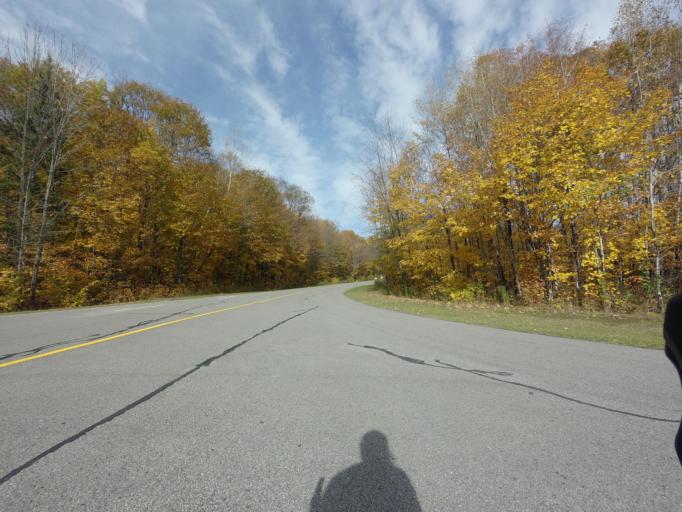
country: CA
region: Quebec
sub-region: Outaouais
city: Gatineau
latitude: 45.4968
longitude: -75.8327
